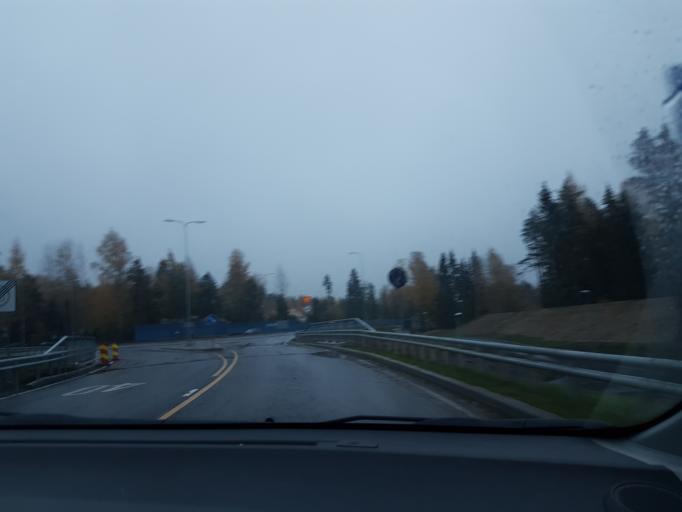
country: FI
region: Uusimaa
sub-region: Helsinki
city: Tuusula
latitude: 60.4042
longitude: 24.9955
